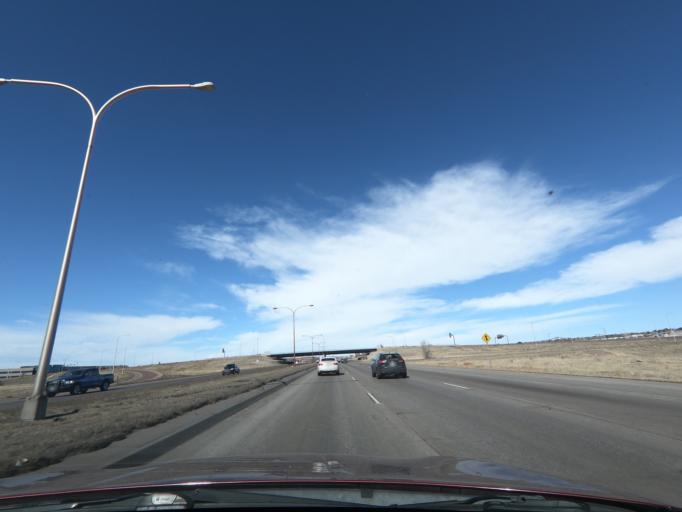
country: US
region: Colorado
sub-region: El Paso County
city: Cimarron Hills
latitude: 38.8365
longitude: -104.7207
